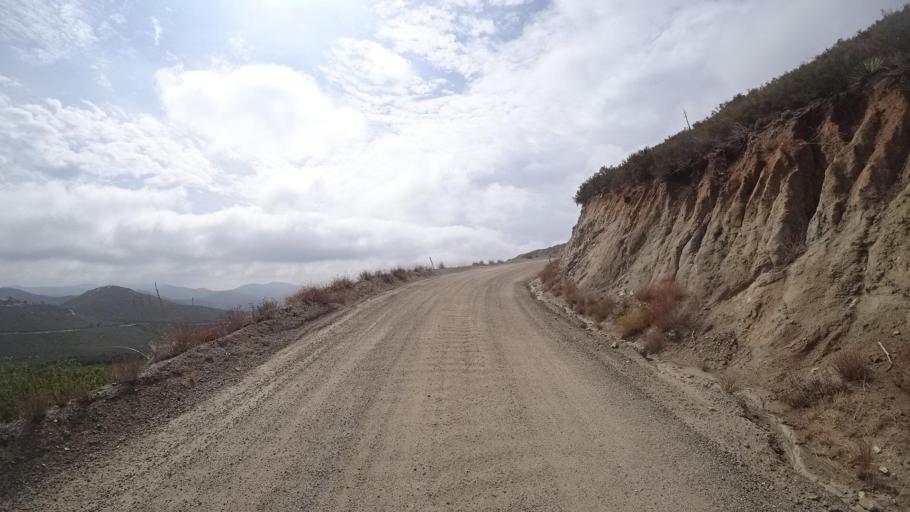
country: US
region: California
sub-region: San Diego County
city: Descanso
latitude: 32.9254
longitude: -116.6328
